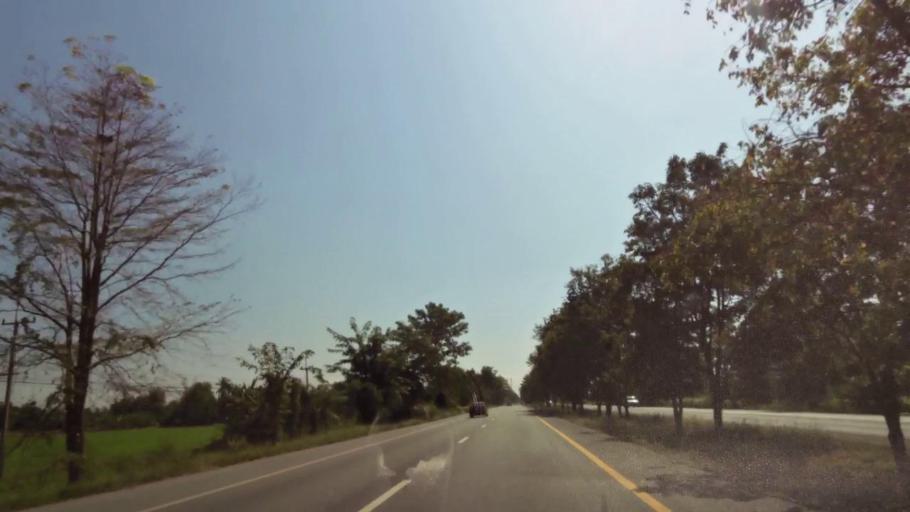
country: TH
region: Nakhon Sawan
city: Kao Liao
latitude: 15.8834
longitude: 100.1153
